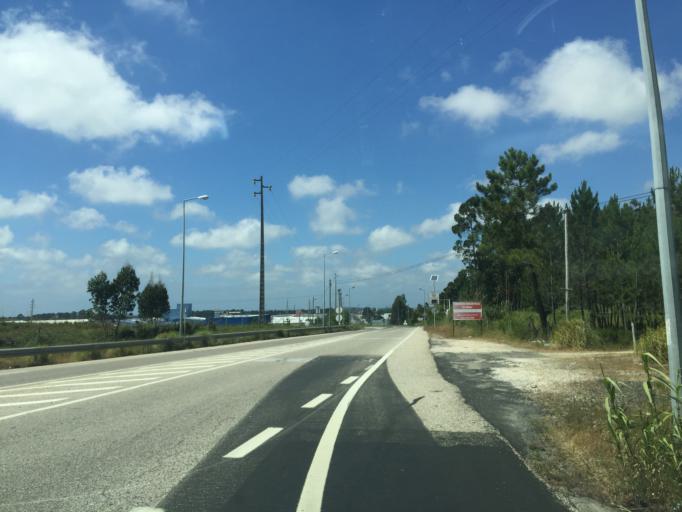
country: PT
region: Leiria
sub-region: Marinha Grande
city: Marinha Grande
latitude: 39.7161
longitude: -8.9243
